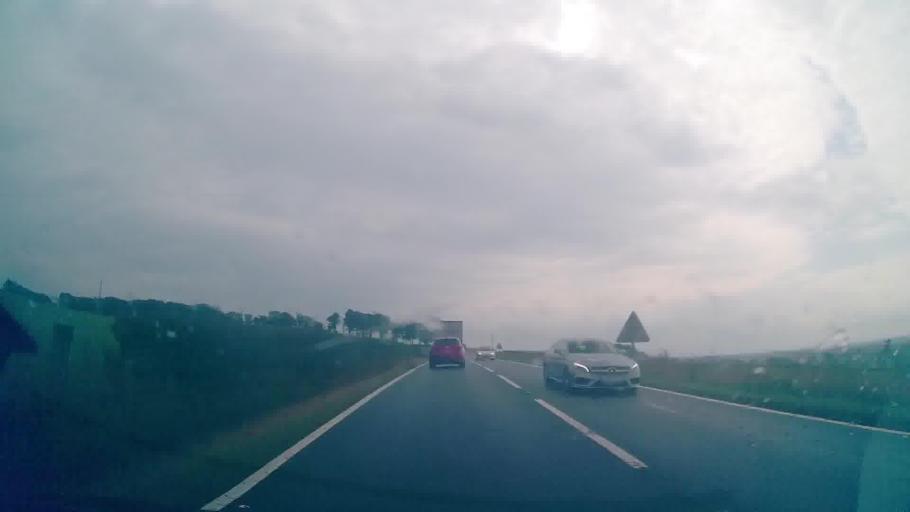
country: GB
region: Scotland
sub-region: Dumfries and Galloway
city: Lochmaben
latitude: 55.0511
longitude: -3.4619
